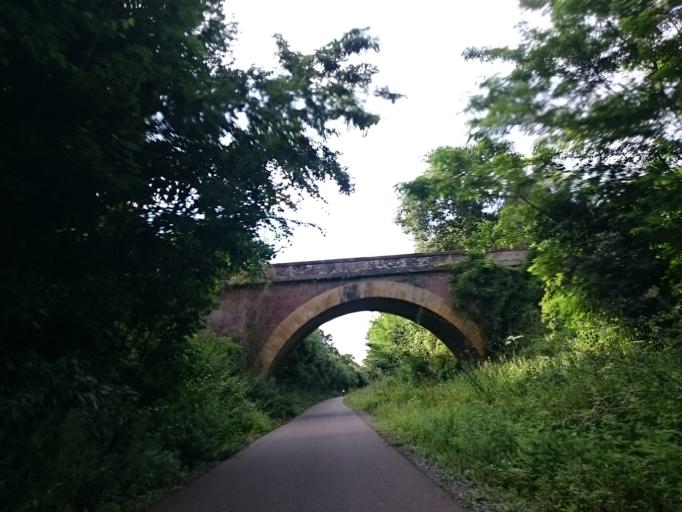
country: FR
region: Lower Normandy
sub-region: Departement du Calvados
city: Saint-Andre-sur-Orne
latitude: 49.1205
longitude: -0.3966
